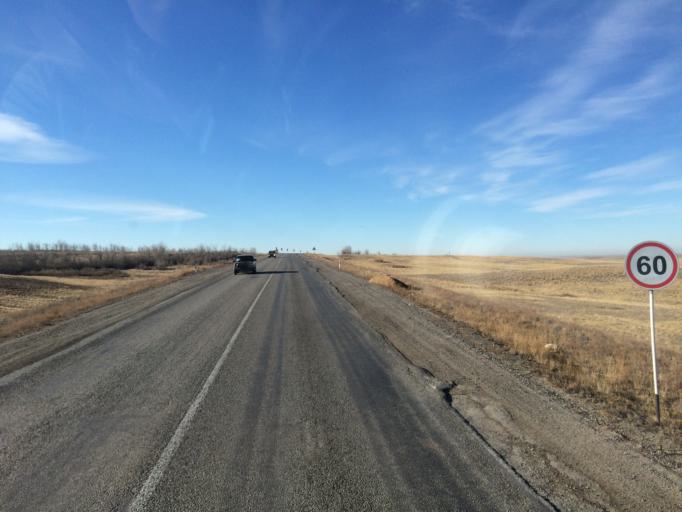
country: KZ
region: Aqtoebe
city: Aqtobe
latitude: 50.2822
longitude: 57.7548
